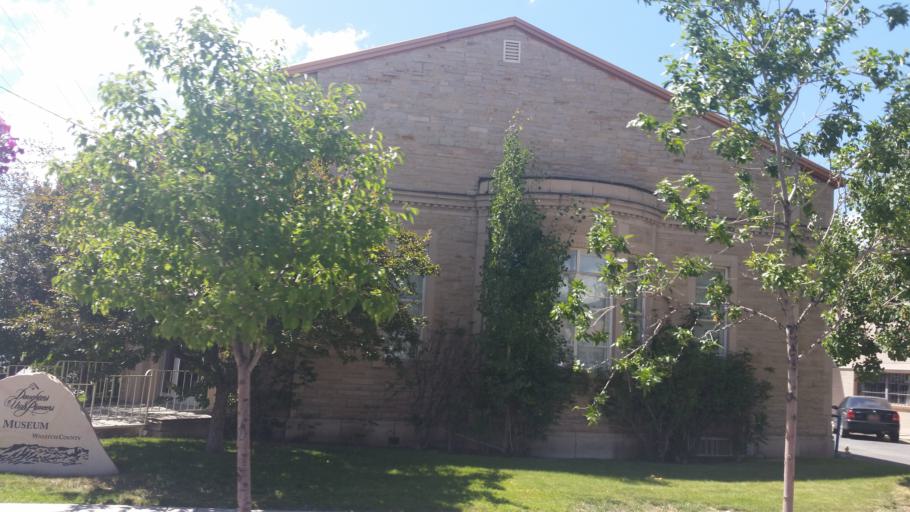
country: US
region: Utah
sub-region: Wasatch County
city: Heber
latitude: 40.5053
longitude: -111.4136
